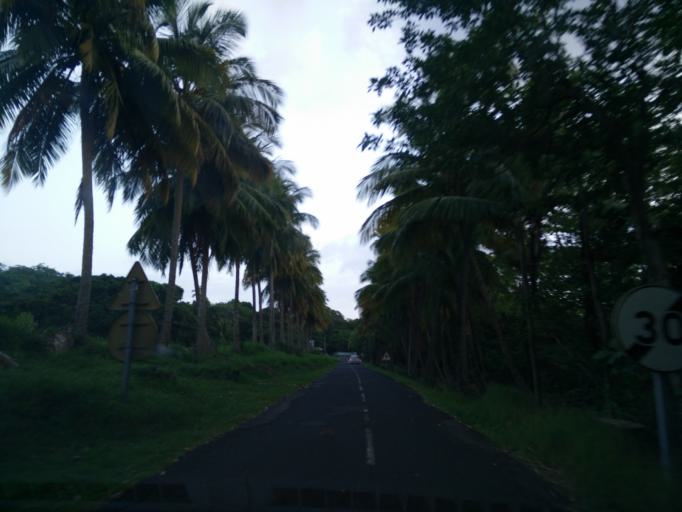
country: MQ
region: Martinique
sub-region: Martinique
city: Saint-Pierre
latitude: 14.8328
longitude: -61.2244
